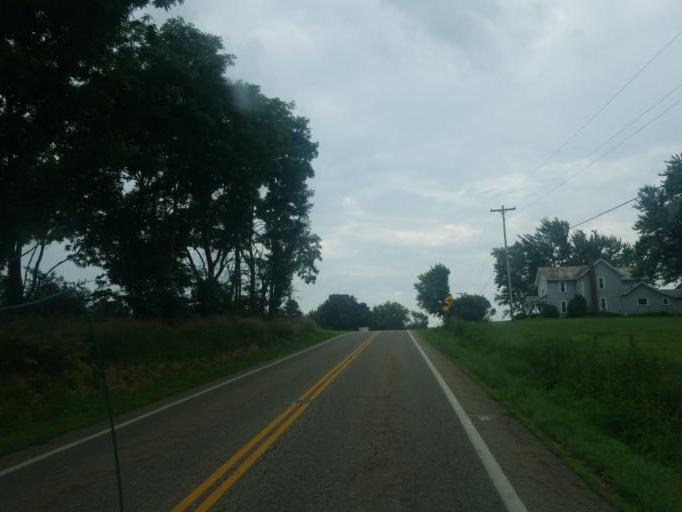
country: US
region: Ohio
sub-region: Carroll County
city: Lake Mohawk
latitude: 40.6356
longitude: -81.2156
